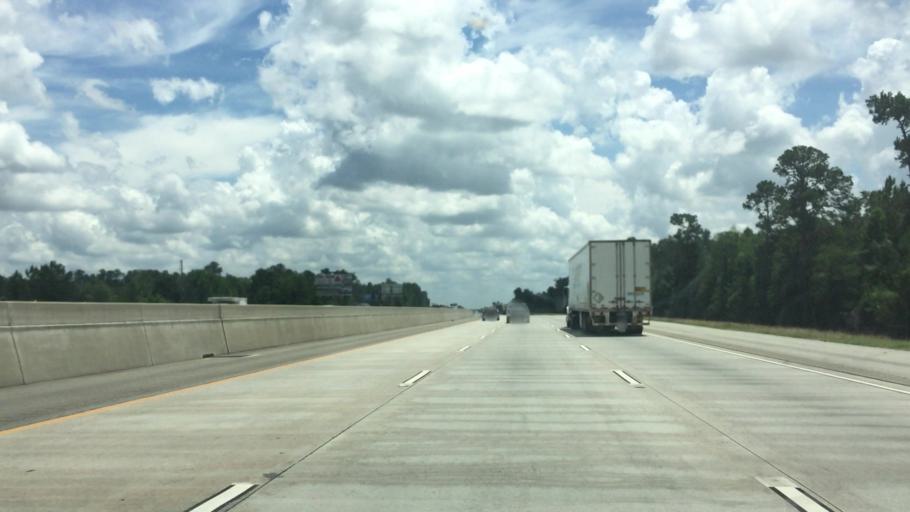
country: US
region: Georgia
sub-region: Cook County
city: Sparks
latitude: 31.2066
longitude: -83.4587
